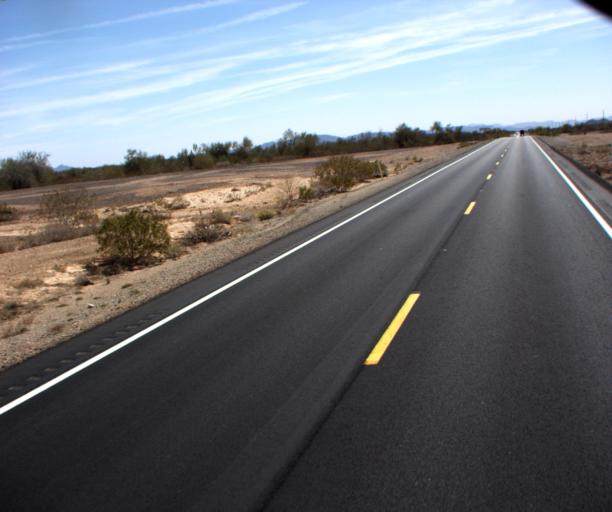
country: US
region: Arizona
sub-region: Yuma County
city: Wellton
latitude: 32.9924
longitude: -114.2873
